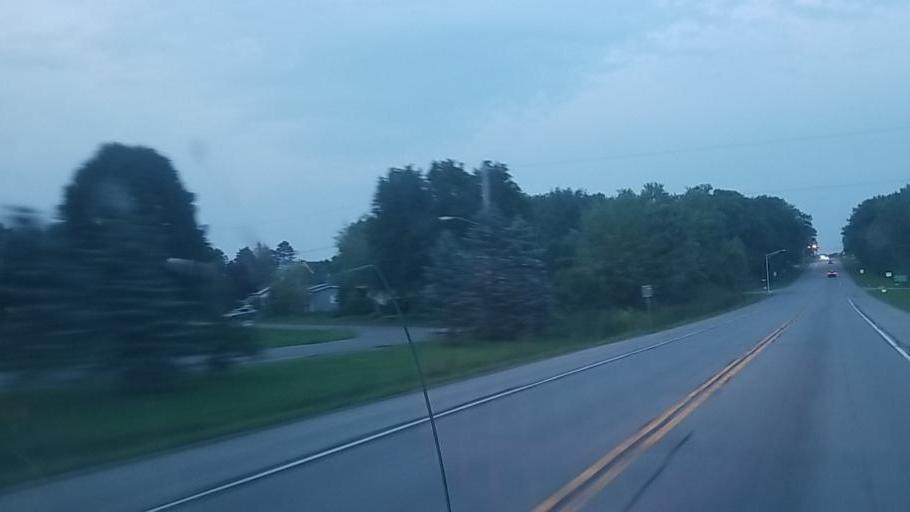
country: US
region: New York
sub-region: Fulton County
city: Johnstown
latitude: 42.9945
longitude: -74.3724
